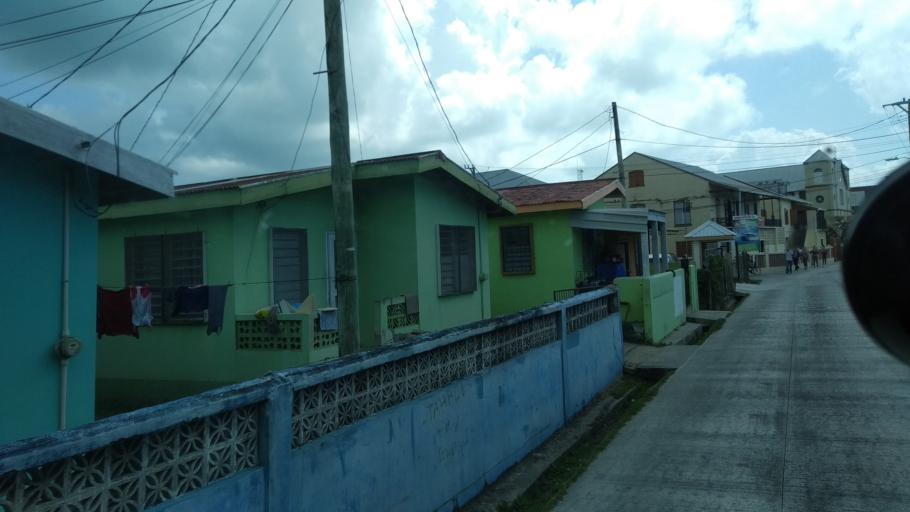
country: BZ
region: Belize
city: Belize City
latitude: 17.4970
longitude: -88.1881
